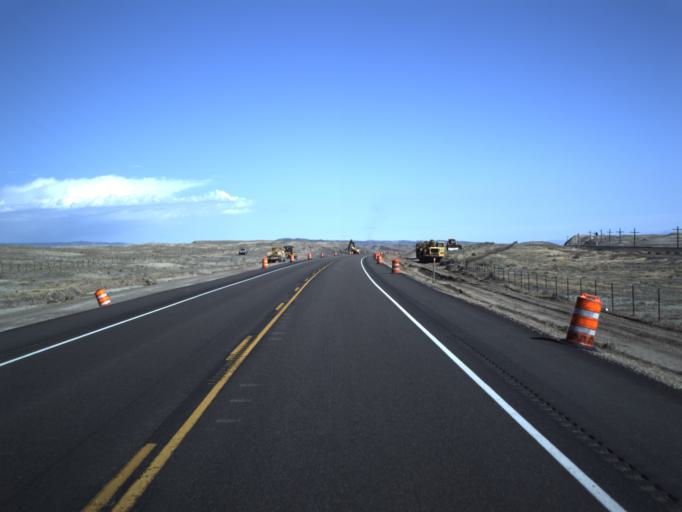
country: US
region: Utah
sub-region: Carbon County
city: East Carbon City
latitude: 39.0290
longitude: -110.3024
